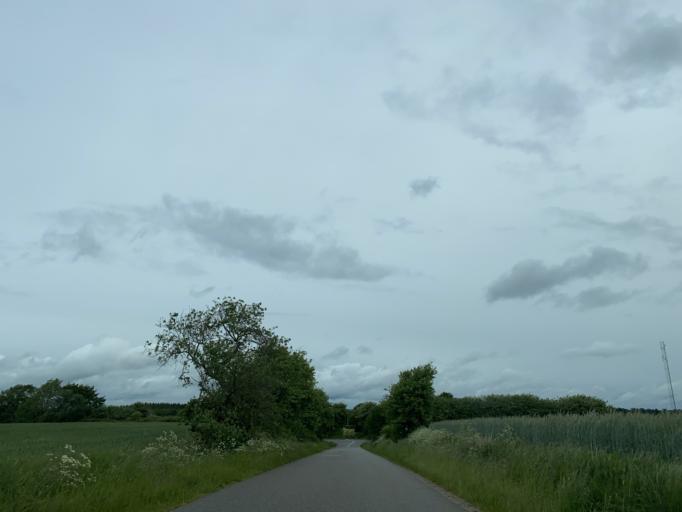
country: DK
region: Central Jutland
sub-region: Favrskov Kommune
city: Hammel
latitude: 56.2408
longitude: 9.7964
